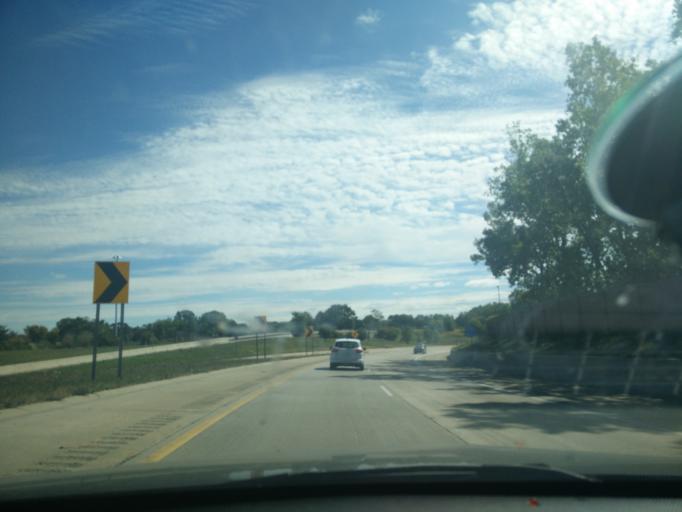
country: US
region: Michigan
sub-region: Macomb County
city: Roseville
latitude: 42.4941
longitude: -82.9191
